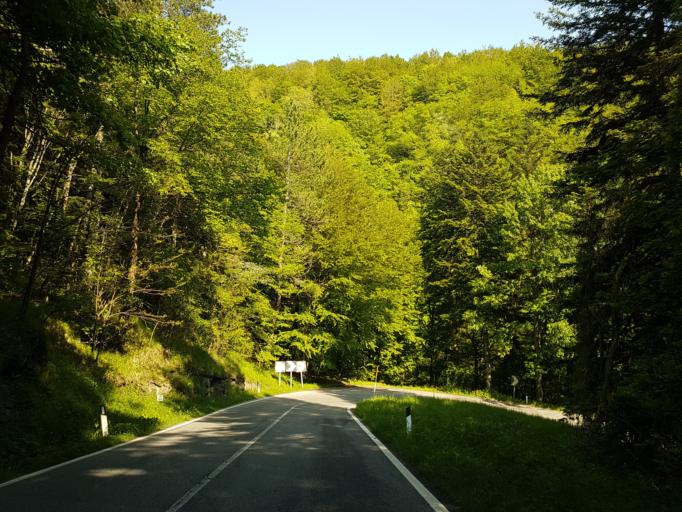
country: IT
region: Tuscany
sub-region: Province of Arezzo
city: Soci
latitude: 43.7960
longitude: 11.8896
